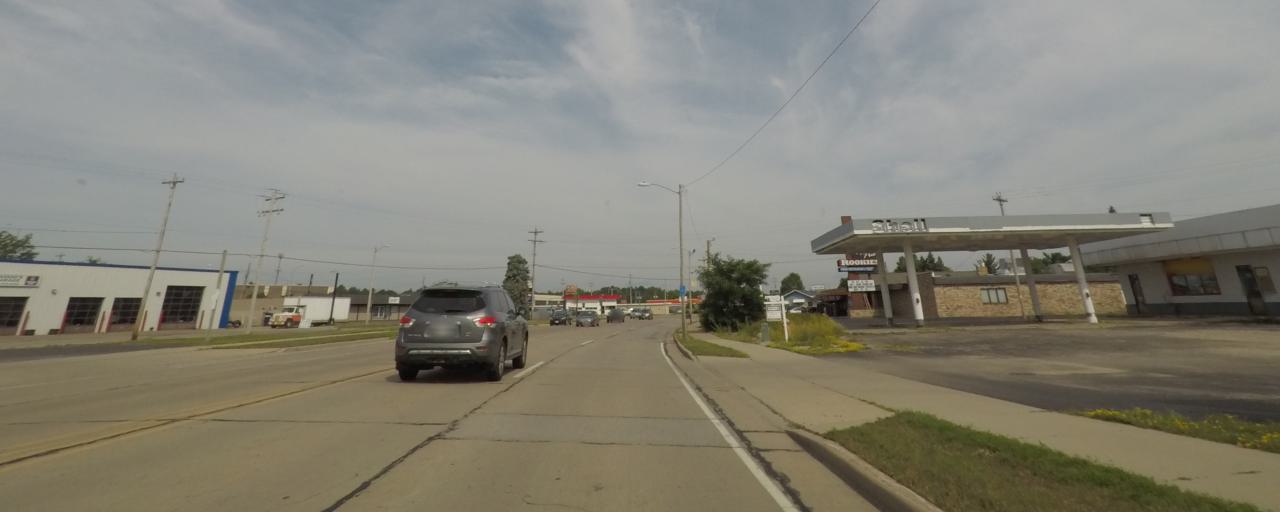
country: US
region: Wisconsin
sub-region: Portage County
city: Whiting
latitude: 44.4981
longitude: -89.5612
